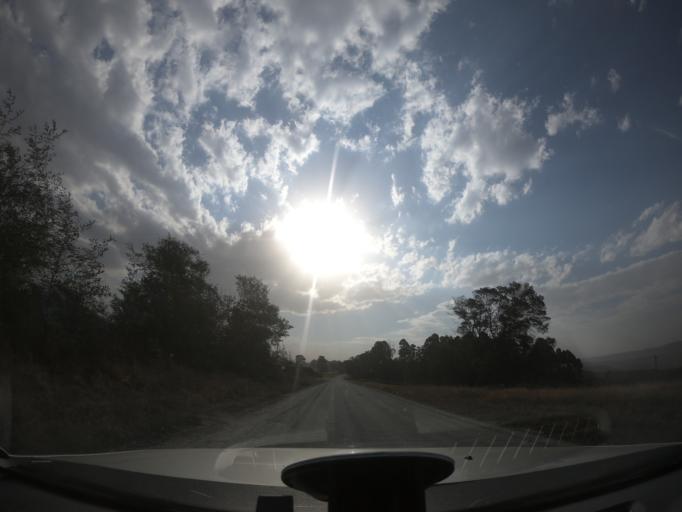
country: ZA
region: KwaZulu-Natal
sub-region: uMgungundlovu District Municipality
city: Howick
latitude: -29.4330
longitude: 30.1115
